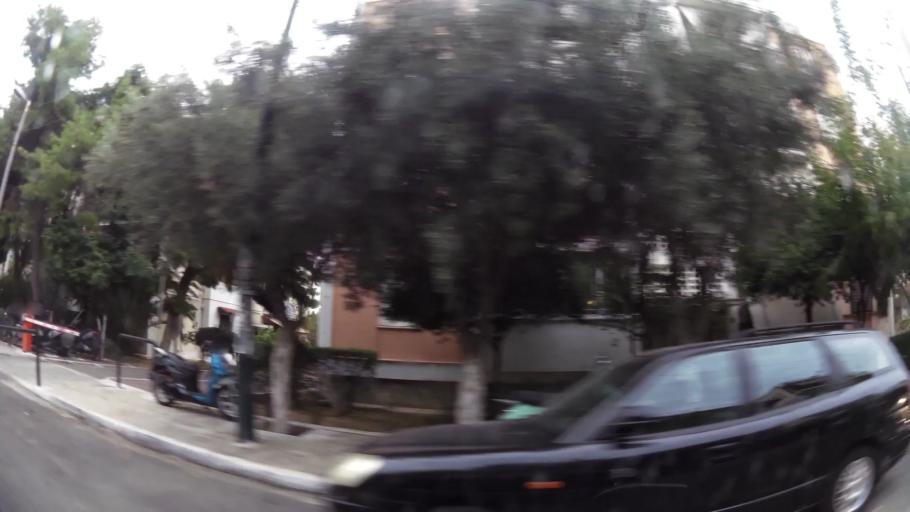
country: GR
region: Attica
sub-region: Nomos Piraios
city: Agios Ioannis Rentis
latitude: 37.9609
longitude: 23.6694
